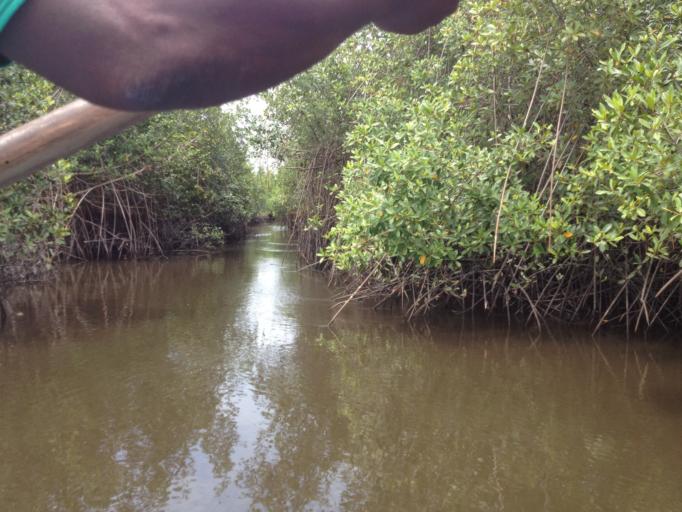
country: BJ
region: Mono
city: Grand-Popo
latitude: 6.3124
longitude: 1.9140
